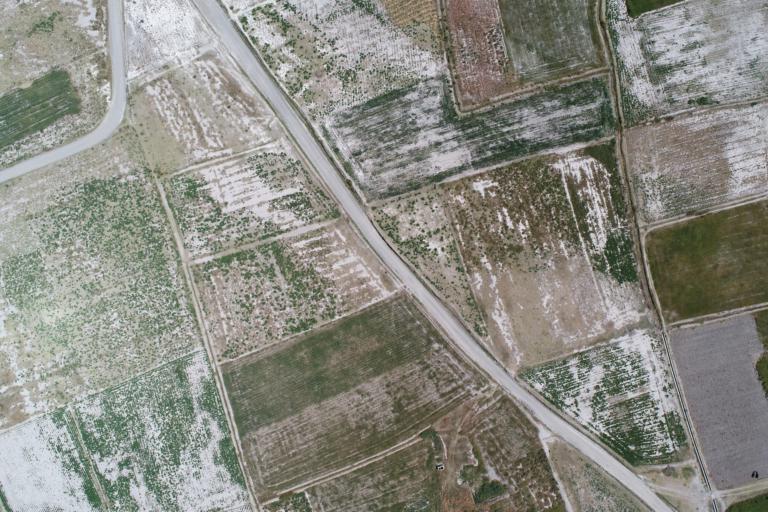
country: BO
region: La Paz
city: Achacachi
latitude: -16.0133
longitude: -68.7235
